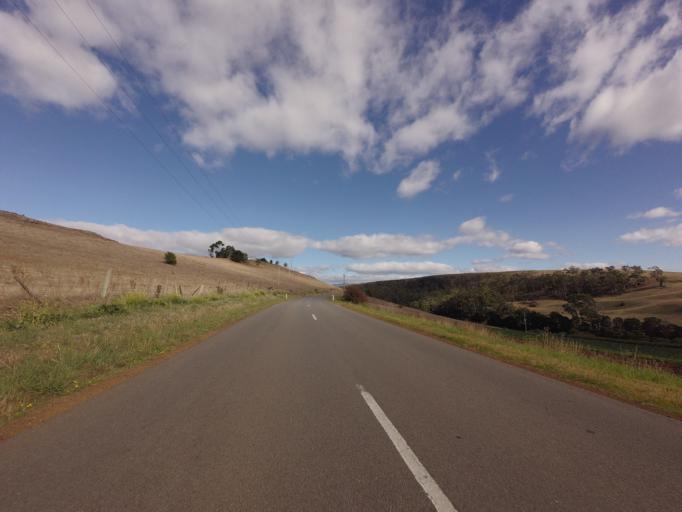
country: AU
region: Tasmania
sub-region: Derwent Valley
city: New Norfolk
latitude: -42.6979
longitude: 146.9275
